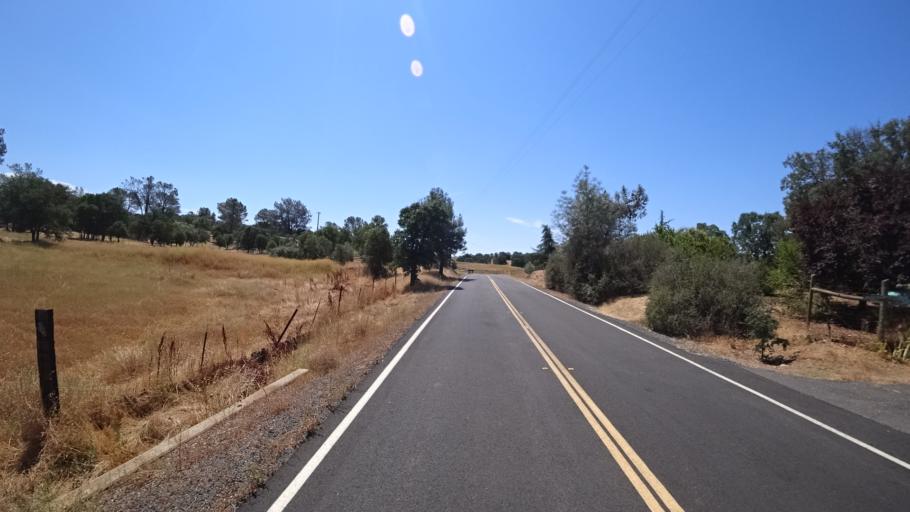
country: US
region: California
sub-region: Calaveras County
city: Copperopolis
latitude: 37.9424
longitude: -120.6205
